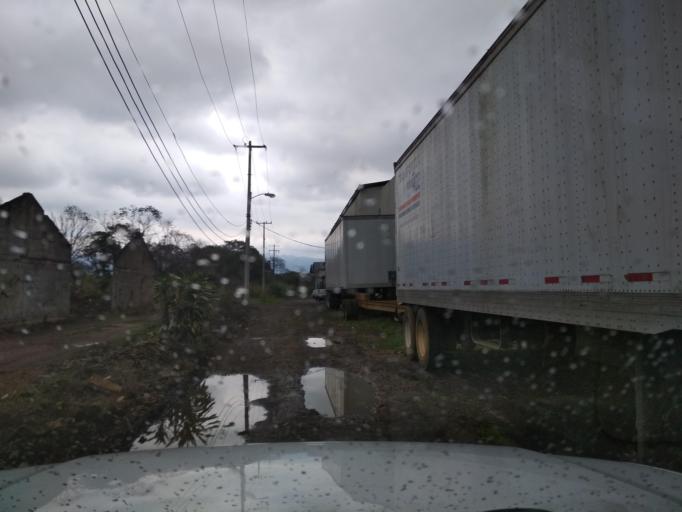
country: MX
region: Veracruz
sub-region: Cordoba
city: Veinte de Noviembre
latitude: 18.8718
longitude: -96.9544
